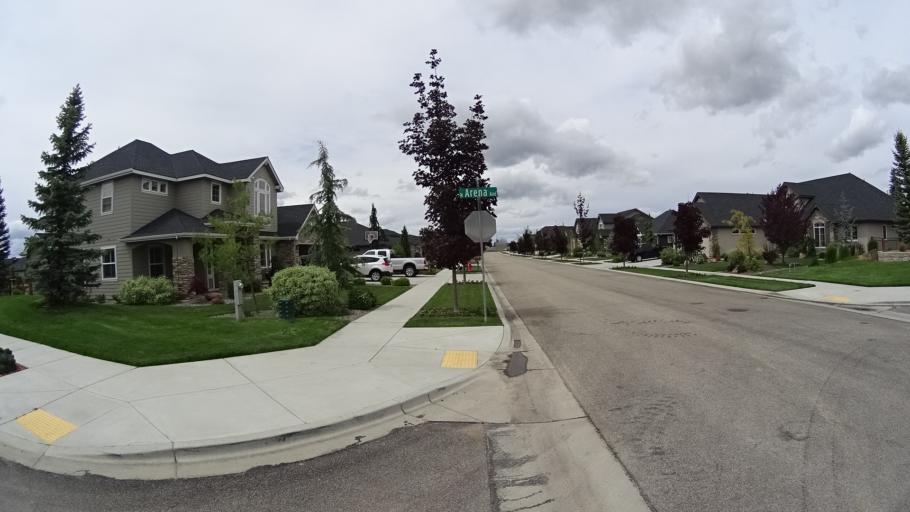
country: US
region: Idaho
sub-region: Ada County
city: Star
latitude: 43.7070
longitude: -116.4305
